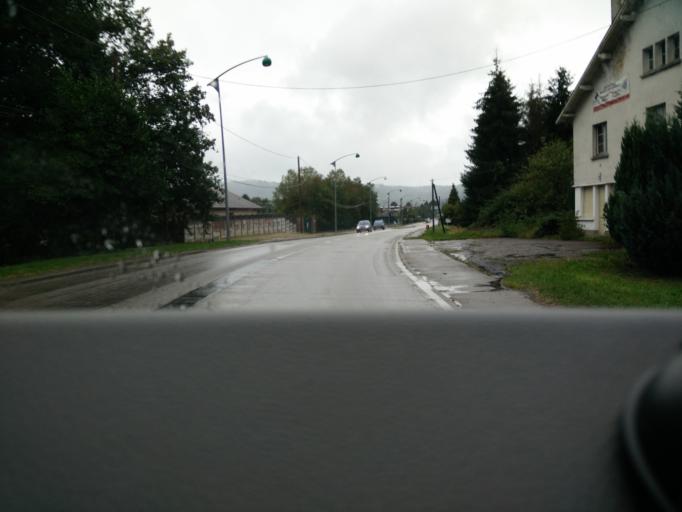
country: FR
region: Lorraine
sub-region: Departement des Vosges
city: Anould
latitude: 48.1849
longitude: 6.9617
